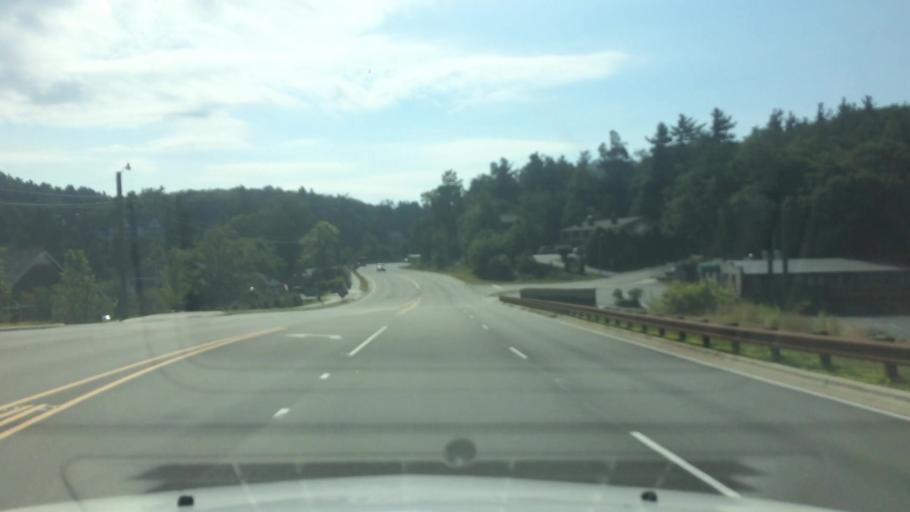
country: US
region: North Carolina
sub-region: Watauga County
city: Blowing Rock
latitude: 36.1206
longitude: -81.6661
